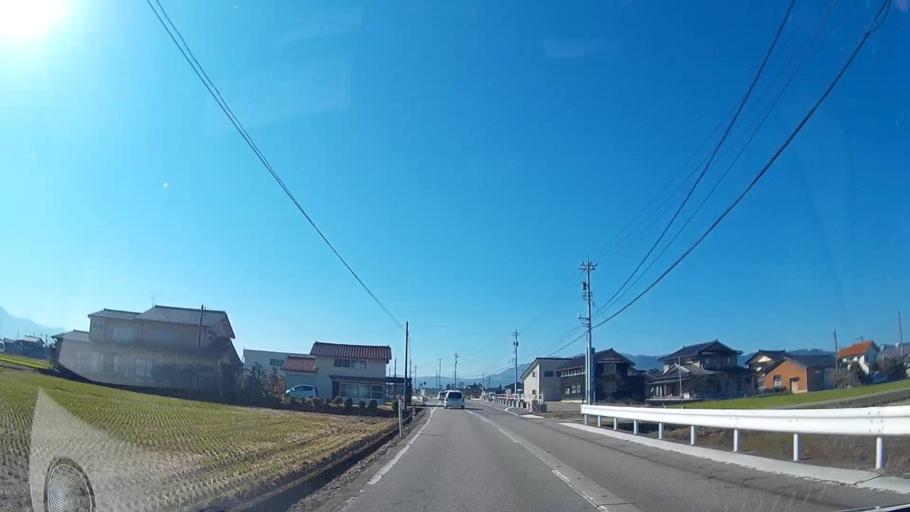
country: JP
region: Toyama
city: Nanto-shi
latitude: 36.5724
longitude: 136.8901
